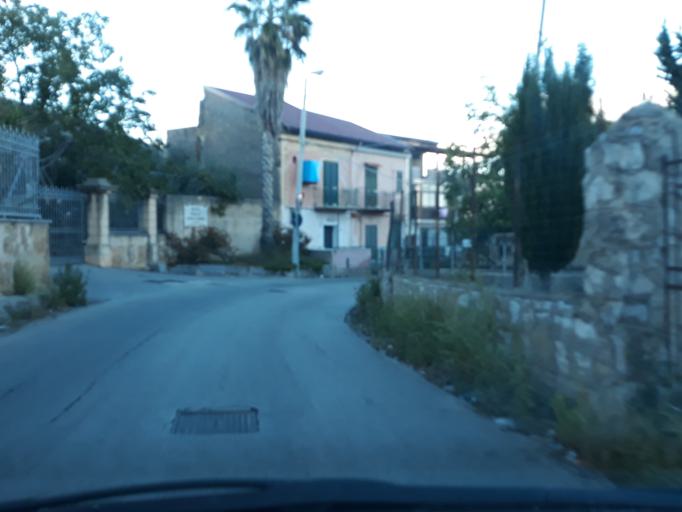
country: IT
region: Sicily
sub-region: Palermo
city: Monreale
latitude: 38.0754
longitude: 13.3102
